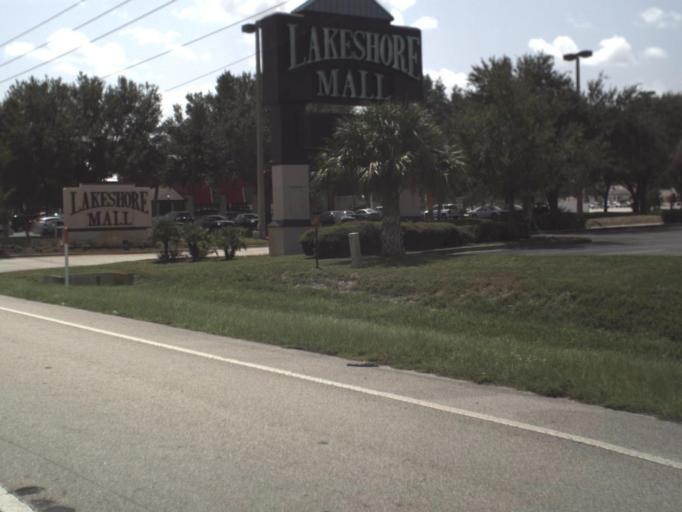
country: US
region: Florida
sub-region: Highlands County
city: Sebring
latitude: 27.4916
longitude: -81.4846
